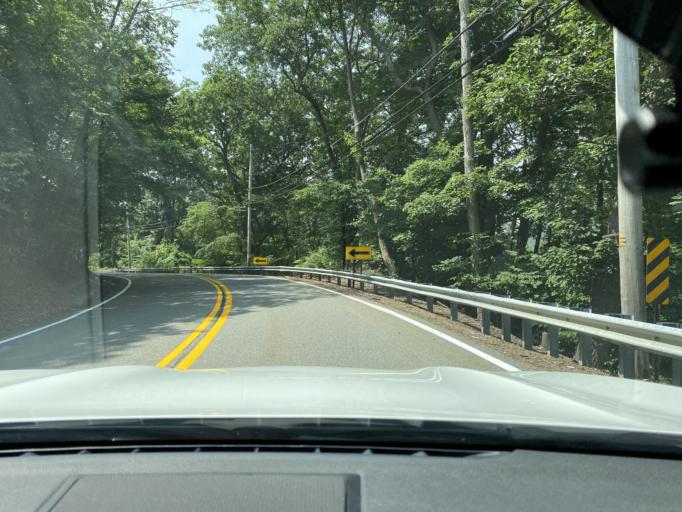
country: US
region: New Jersey
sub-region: Bergen County
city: Franklin Lakes
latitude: 41.0712
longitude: -74.2018
